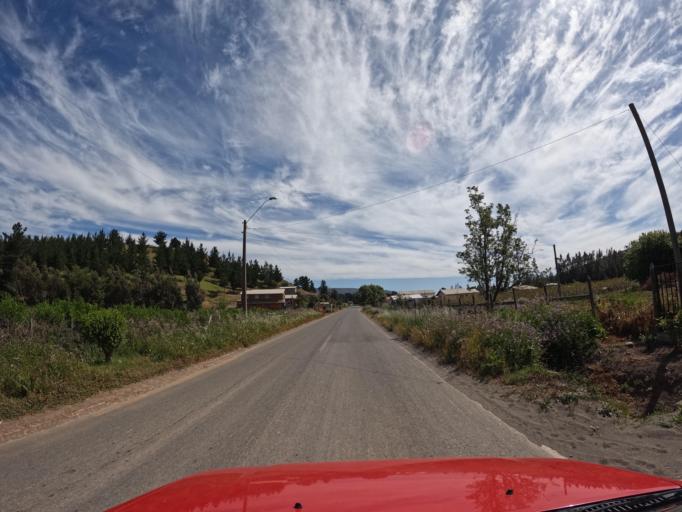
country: CL
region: Maule
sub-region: Provincia de Talca
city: Constitucion
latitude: -35.0288
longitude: -72.0498
